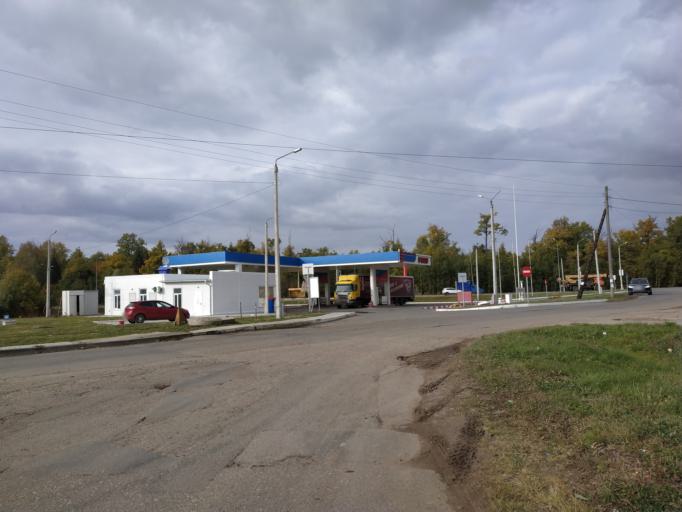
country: RU
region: Chuvashia
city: Ishley
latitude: 56.1327
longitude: 47.0864
